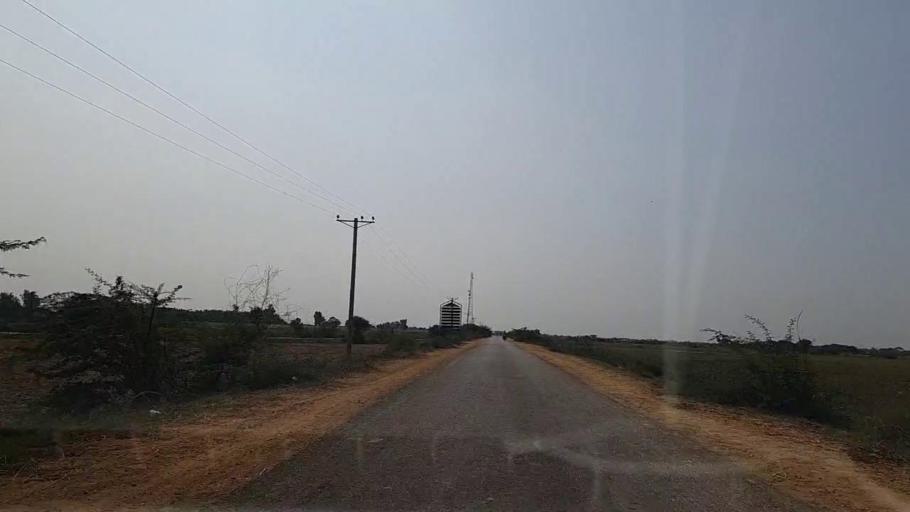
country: PK
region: Sindh
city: Chuhar Jamali
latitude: 24.2887
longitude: 67.9249
